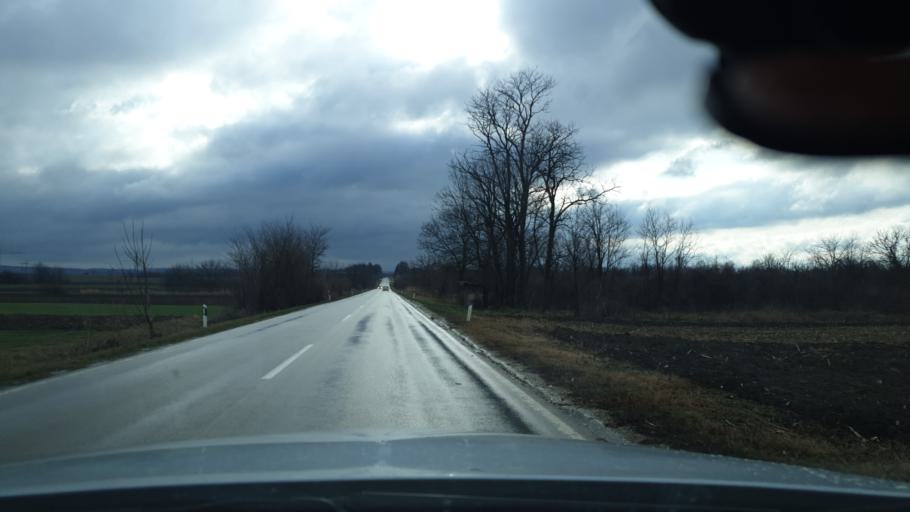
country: RS
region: Central Serbia
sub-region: Branicevski Okrug
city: Malo Crnice
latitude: 44.5394
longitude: 21.3117
